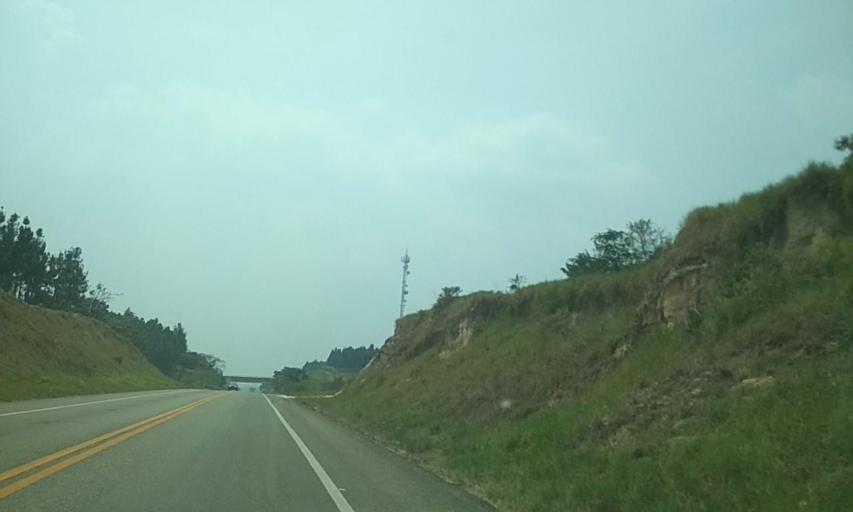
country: MX
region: Tabasco
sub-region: Huimanguillo
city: Francisco Rueda
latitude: 17.7480
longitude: -93.9916
